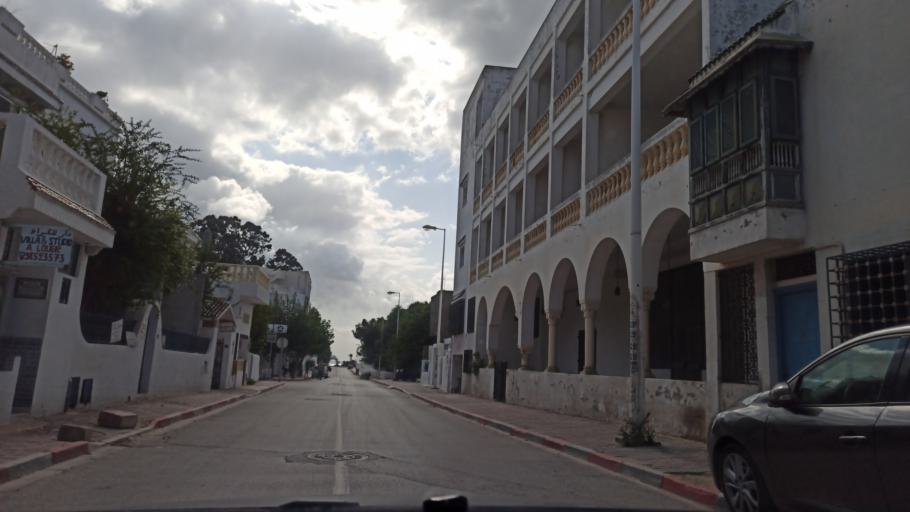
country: TN
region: Nabul
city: Al Hammamat
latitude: 36.3954
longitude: 10.6149
